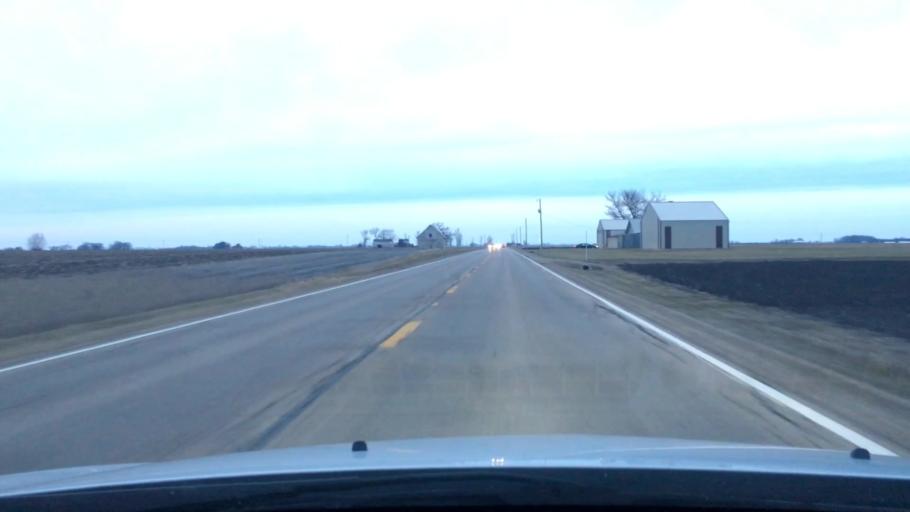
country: US
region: Illinois
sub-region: LaSalle County
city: Peru
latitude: 41.4187
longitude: -89.1263
